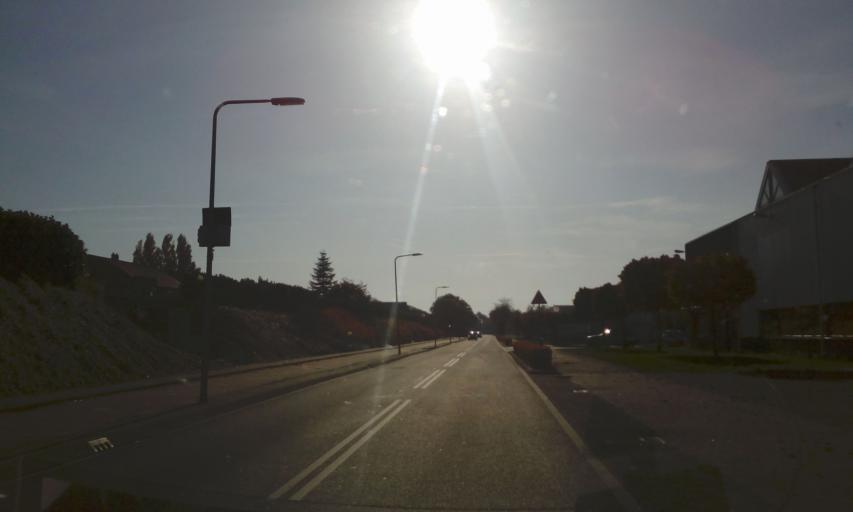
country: NL
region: South Holland
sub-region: Gemeente Lansingerland
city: Bleiswijk
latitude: 52.0152
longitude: 4.5445
